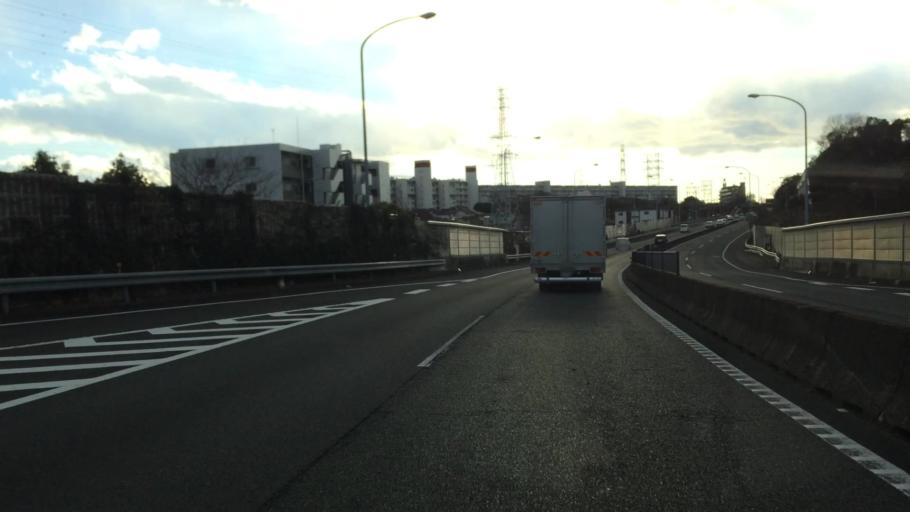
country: JP
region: Kanagawa
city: Yokohama
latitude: 35.4310
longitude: 139.5517
